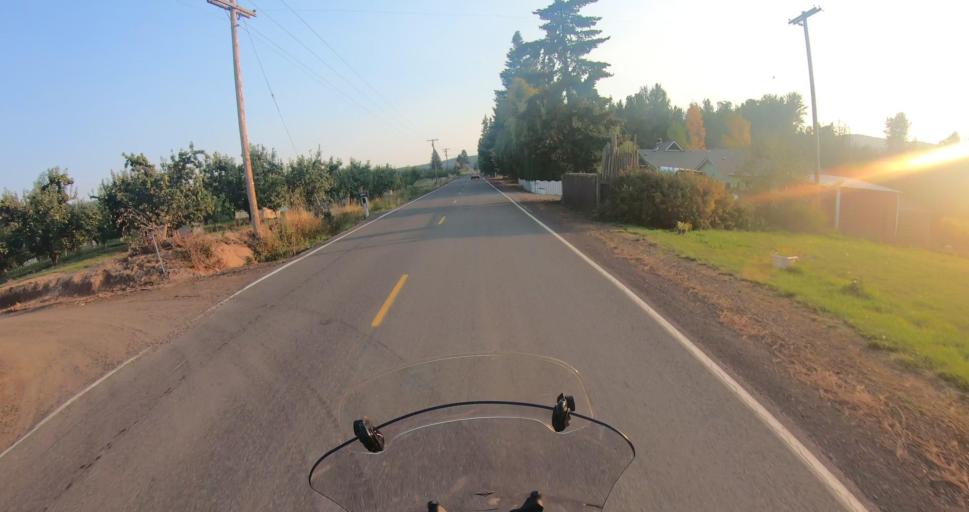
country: US
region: Oregon
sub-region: Hood River County
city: Odell
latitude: 45.5101
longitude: -121.5968
